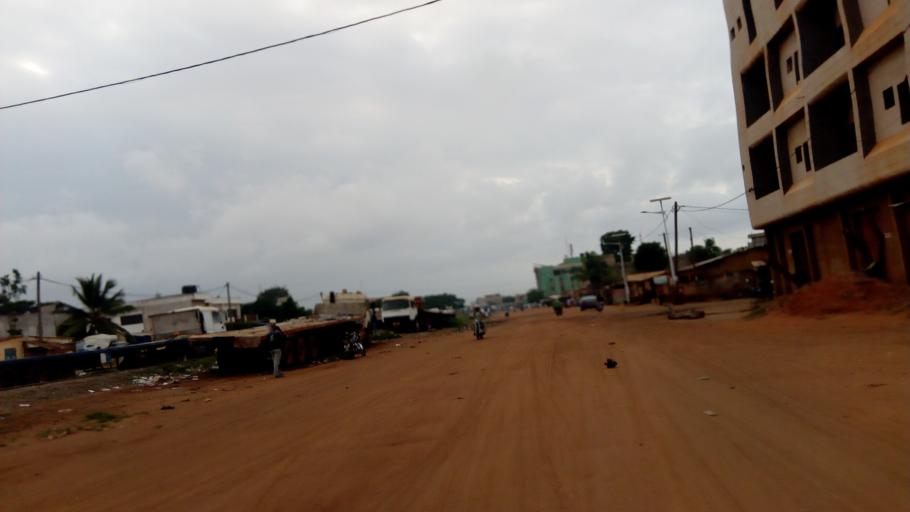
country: TG
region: Maritime
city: Lome
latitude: 6.1654
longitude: 1.2045
